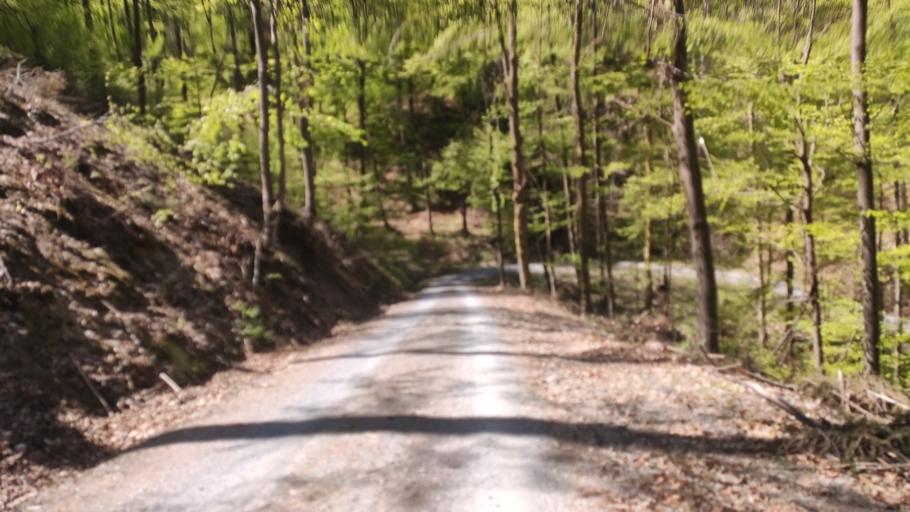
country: DE
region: Bavaria
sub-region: Upper Franconia
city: Nordhalben
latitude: 50.3610
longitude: 11.4764
